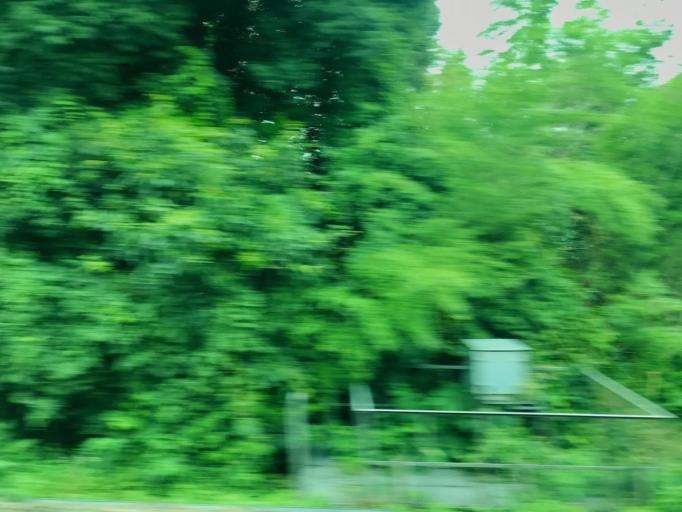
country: JP
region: Tochigi
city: Kuroiso
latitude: 37.0215
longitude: 140.1153
